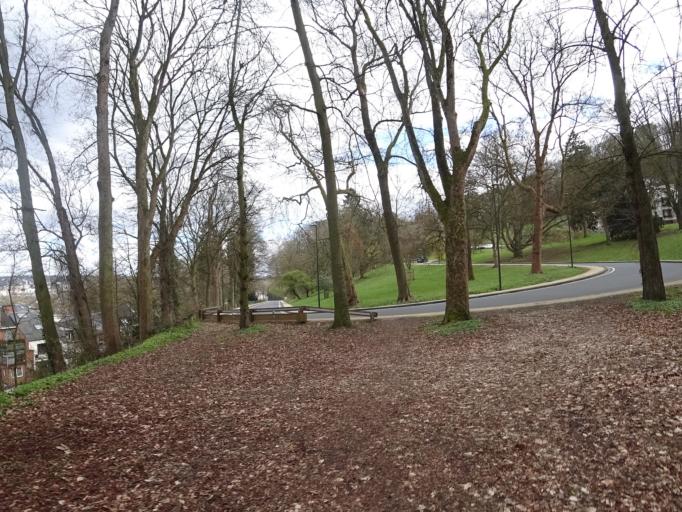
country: BE
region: Wallonia
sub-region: Province de Namur
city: Namur
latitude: 50.4612
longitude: 4.8558
